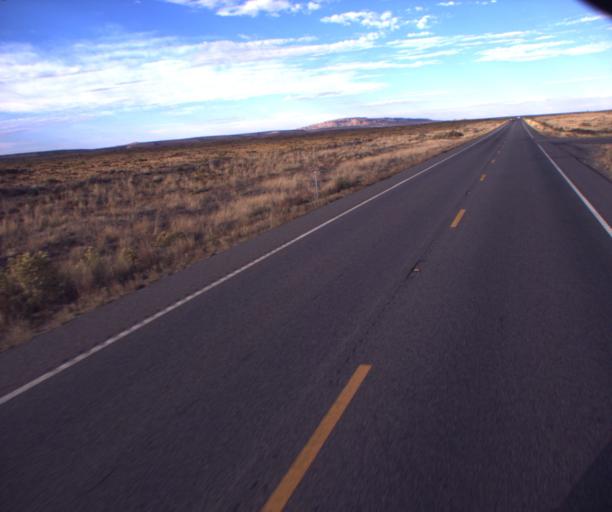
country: US
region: Arizona
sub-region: Apache County
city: Lukachukai
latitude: 36.9285
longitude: -109.2011
